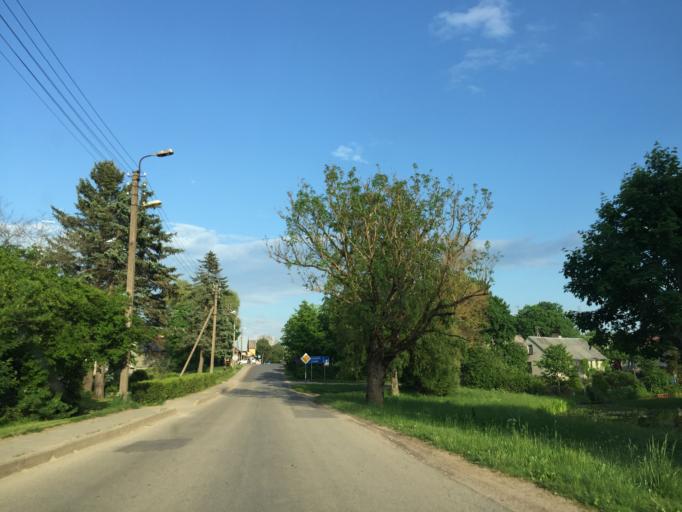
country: LT
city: Plateliai
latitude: 56.0437
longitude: 21.8130
